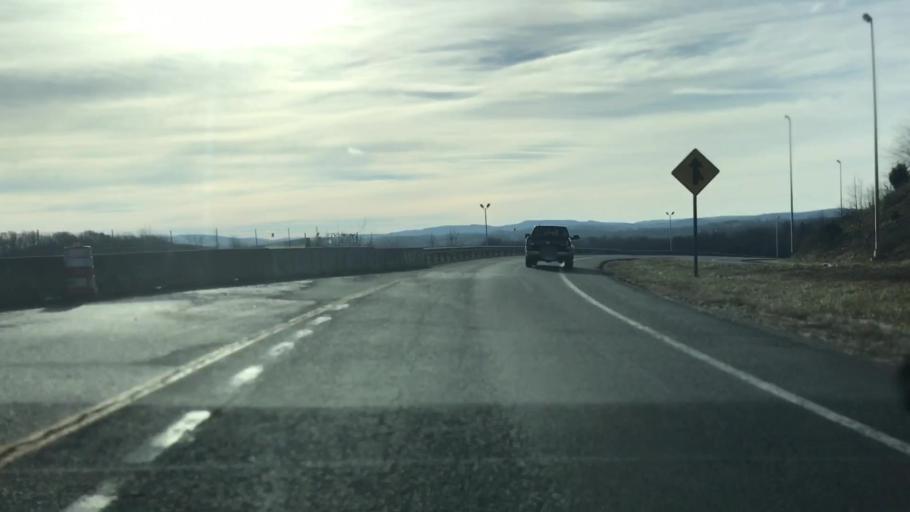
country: US
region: Virginia
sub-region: Montgomery County
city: Merrimac
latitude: 37.1897
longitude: -80.4016
